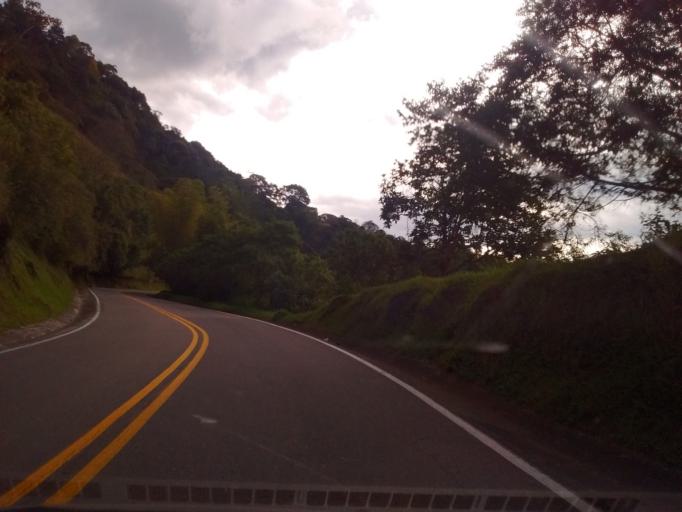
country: CO
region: Huila
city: San Agustin
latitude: 1.8755
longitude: -76.2448
